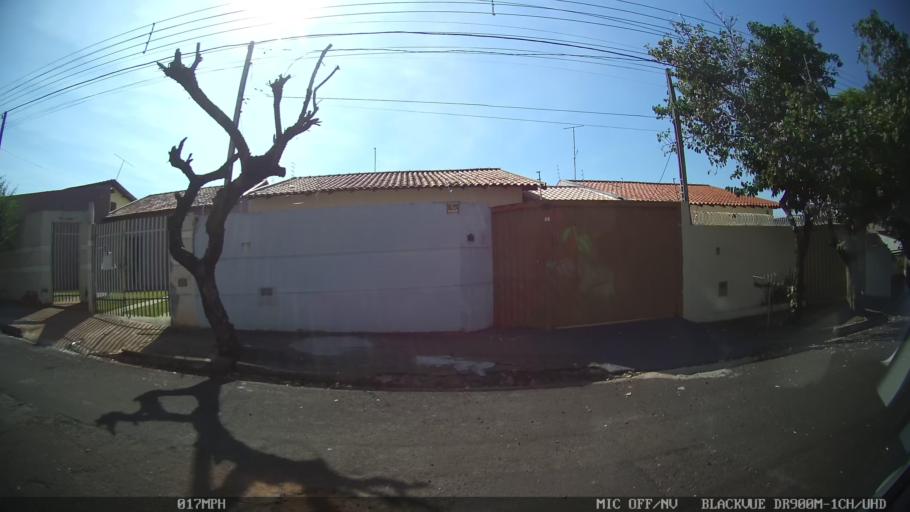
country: BR
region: Sao Paulo
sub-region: Sao Jose Do Rio Preto
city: Sao Jose do Rio Preto
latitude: -20.7882
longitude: -49.4367
